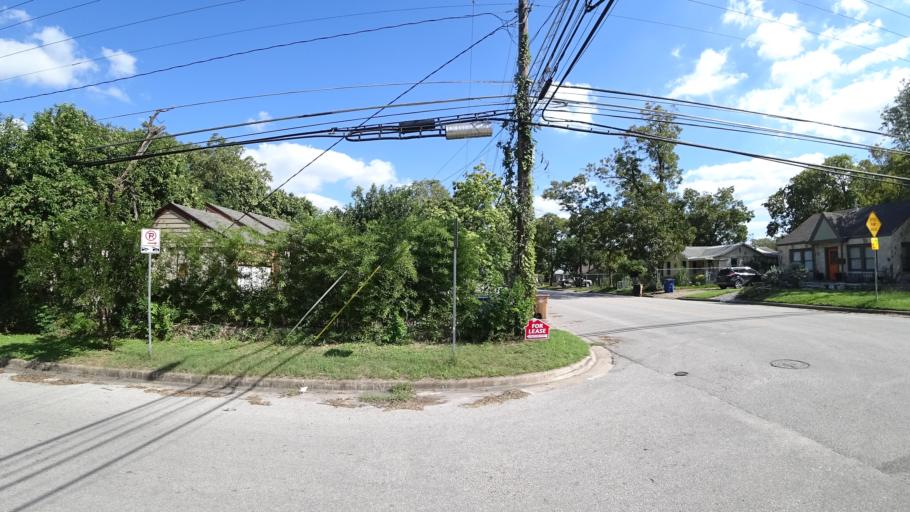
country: US
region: Texas
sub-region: Travis County
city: Austin
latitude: 30.3138
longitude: -97.7118
